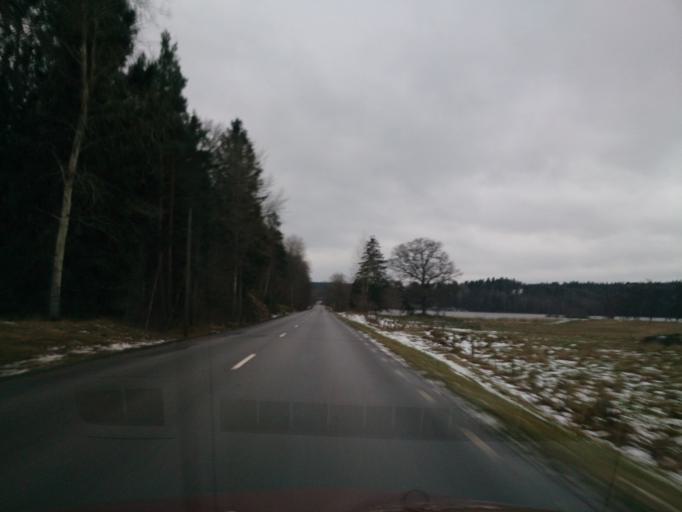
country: SE
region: OEstergoetland
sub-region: Atvidabergs Kommun
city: Atvidaberg
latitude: 58.3448
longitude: 16.0288
